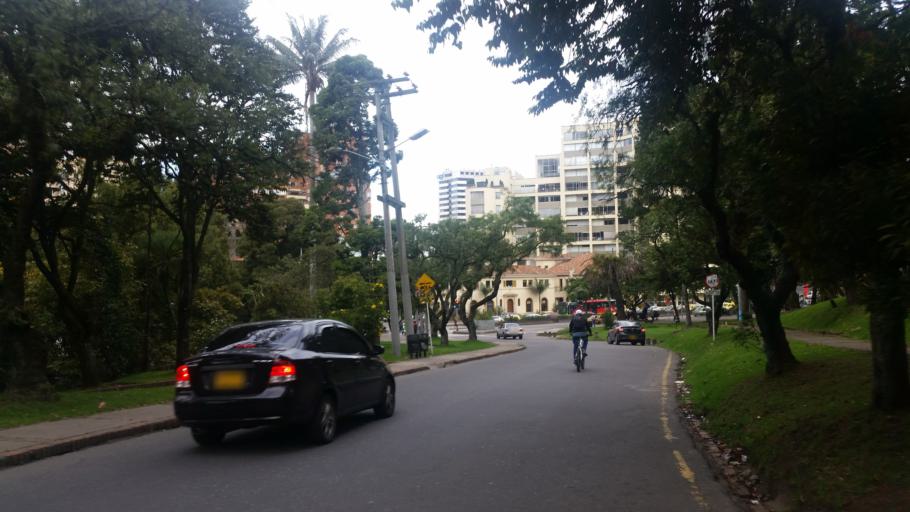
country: CO
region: Bogota D.C.
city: Bogota
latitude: 4.6253
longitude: -74.0651
